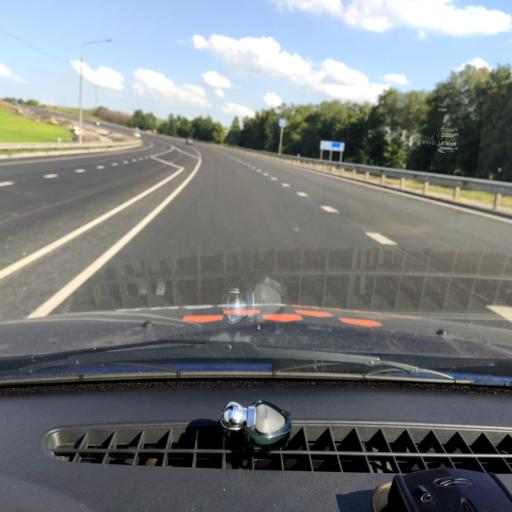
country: RU
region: Lipetsk
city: Yelets
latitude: 52.5800
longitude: 38.5139
